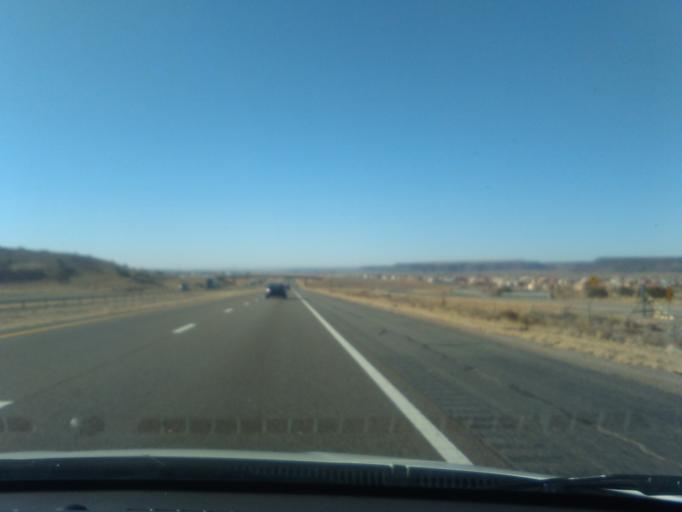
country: US
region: New Mexico
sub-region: Sandoval County
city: San Felipe Pueblo
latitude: 35.4033
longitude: -106.4310
